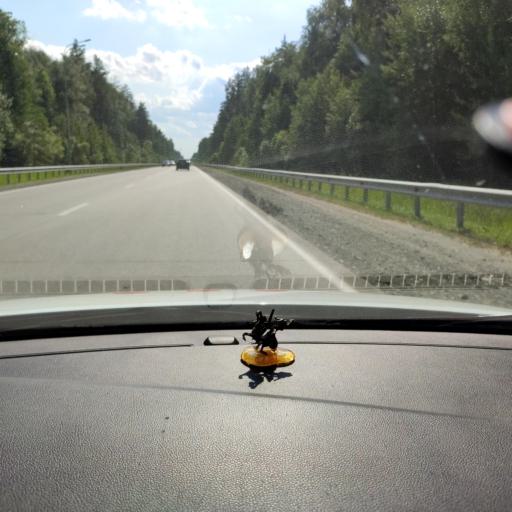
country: RU
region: Tatarstan
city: Stolbishchi
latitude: 55.6646
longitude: 49.1608
